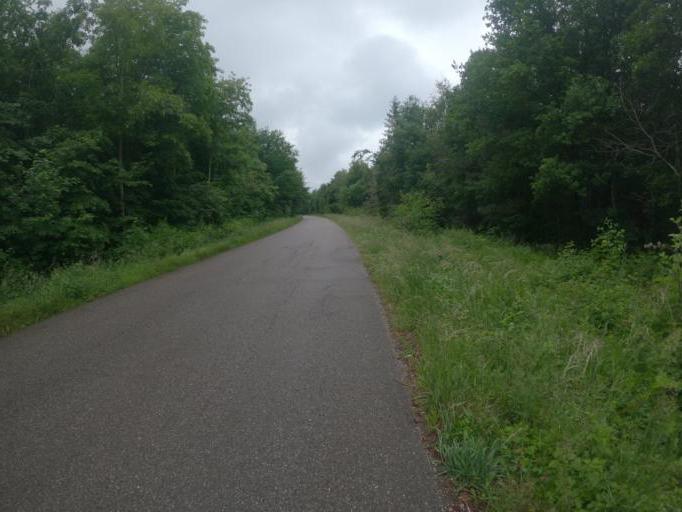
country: DE
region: Baden-Wuerttemberg
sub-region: Regierungsbezirk Stuttgart
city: Adelberg
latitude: 48.7781
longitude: 9.5879
